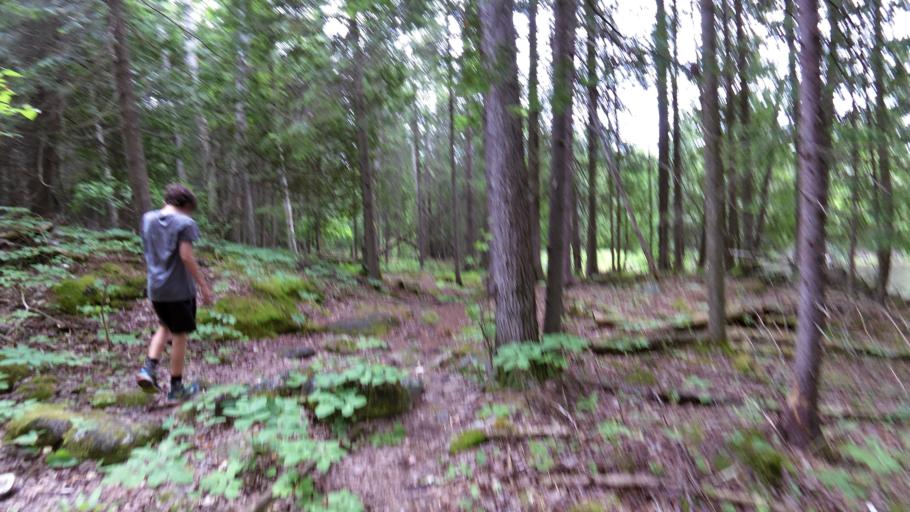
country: CA
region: Ontario
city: Arnprior
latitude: 45.4608
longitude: -76.2515
